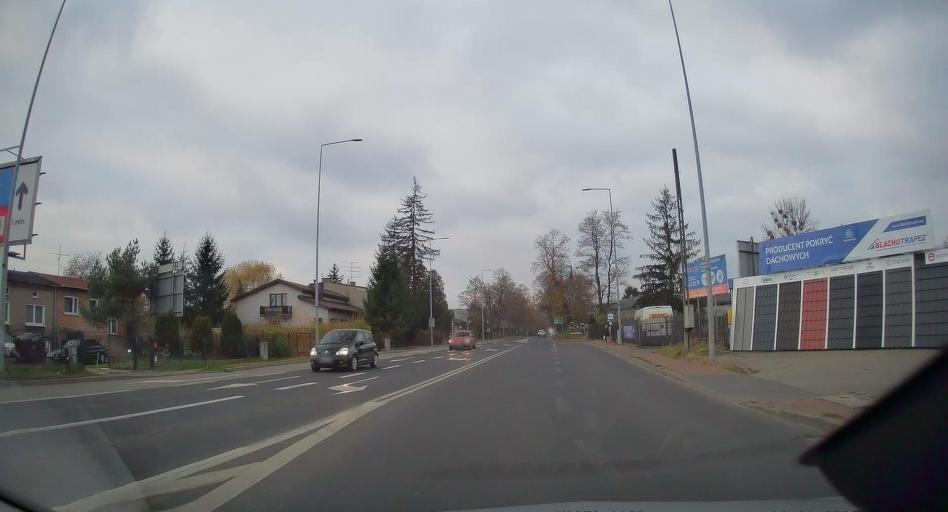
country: PL
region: Silesian Voivodeship
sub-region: Czestochowa
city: Czestochowa
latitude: 50.8229
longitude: 19.0815
